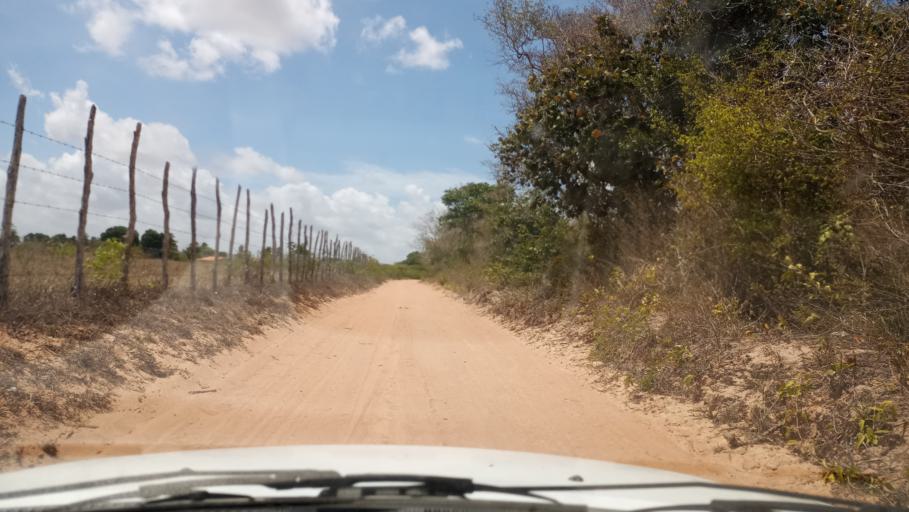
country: BR
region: Rio Grande do Norte
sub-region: Goianinha
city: Goianinha
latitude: -6.2833
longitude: -35.2853
